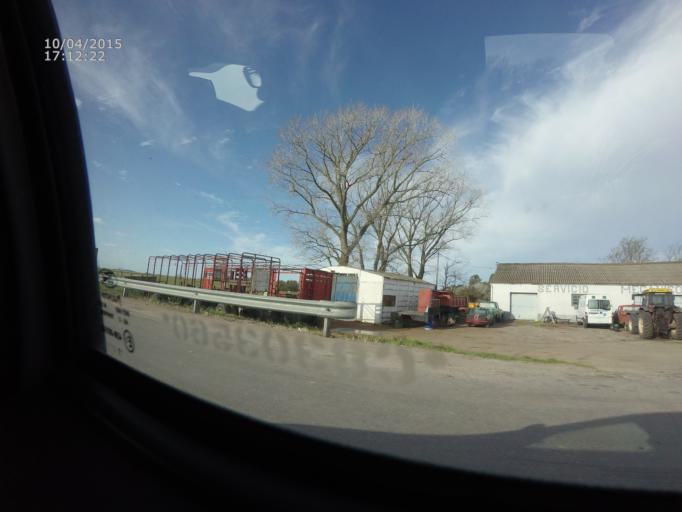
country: AR
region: Buenos Aires
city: Coronel Vidal
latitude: -37.2713
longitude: -57.7674
